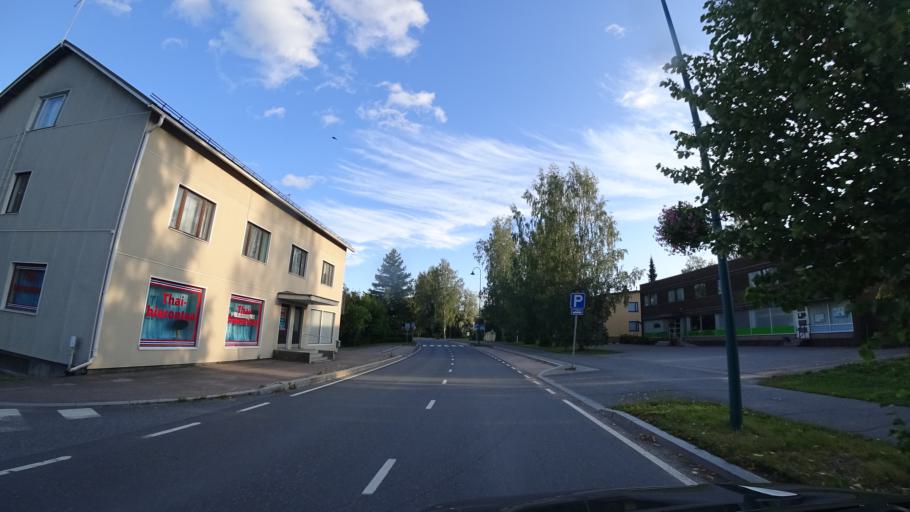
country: FI
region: Haeme
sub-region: Haemeenlinna
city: Lammi
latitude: 61.0770
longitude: 25.0108
